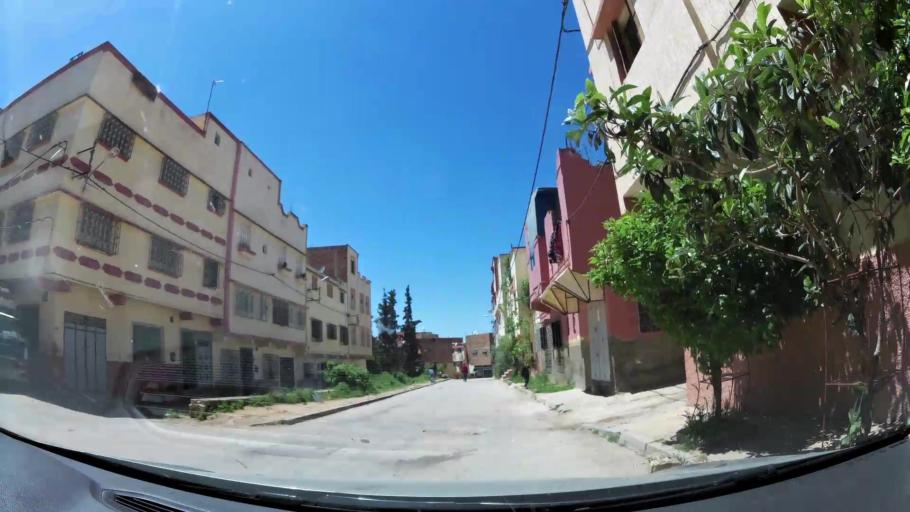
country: MA
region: Meknes-Tafilalet
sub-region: Meknes
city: Meknes
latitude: 33.9064
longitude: -5.5785
